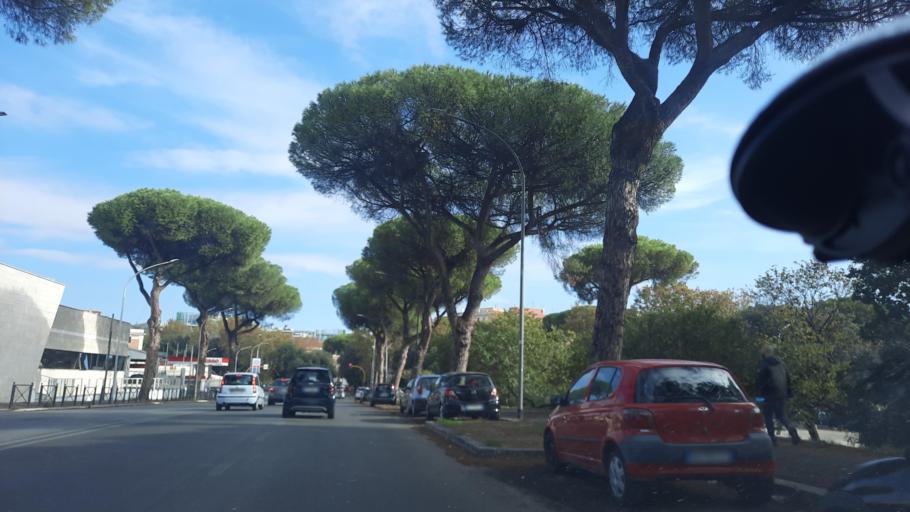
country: IT
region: Latium
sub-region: Citta metropolitana di Roma Capitale
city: Rome
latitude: 41.8617
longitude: 12.4772
